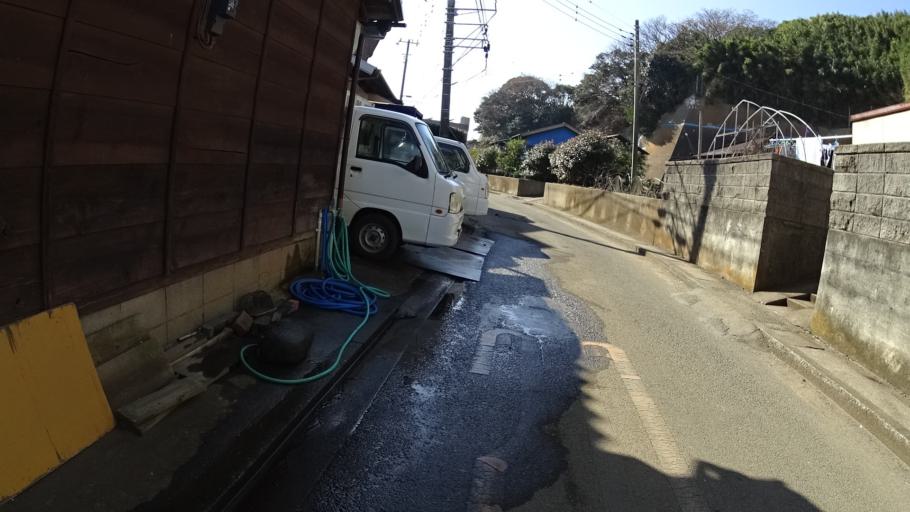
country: JP
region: Kanagawa
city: Miura
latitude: 35.1864
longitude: 139.6216
